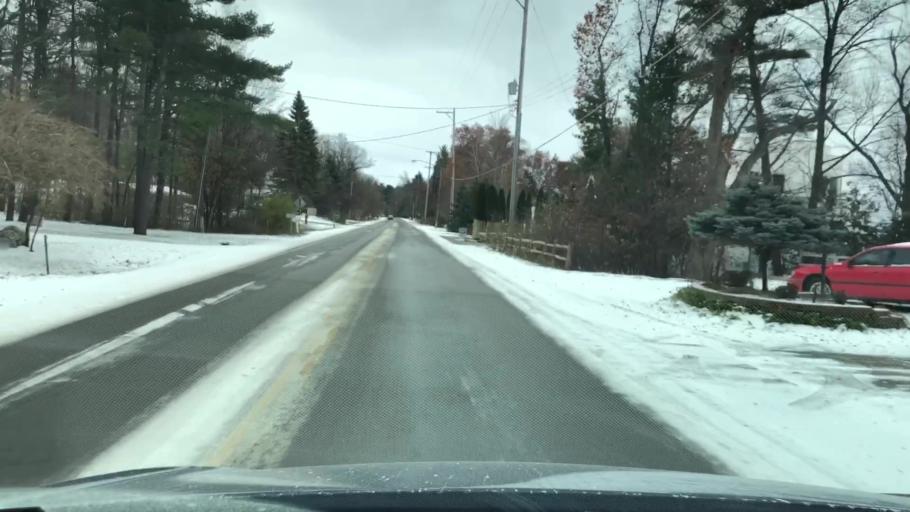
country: US
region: Michigan
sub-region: Grand Traverse County
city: Traverse City
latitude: 44.7819
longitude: -85.5899
